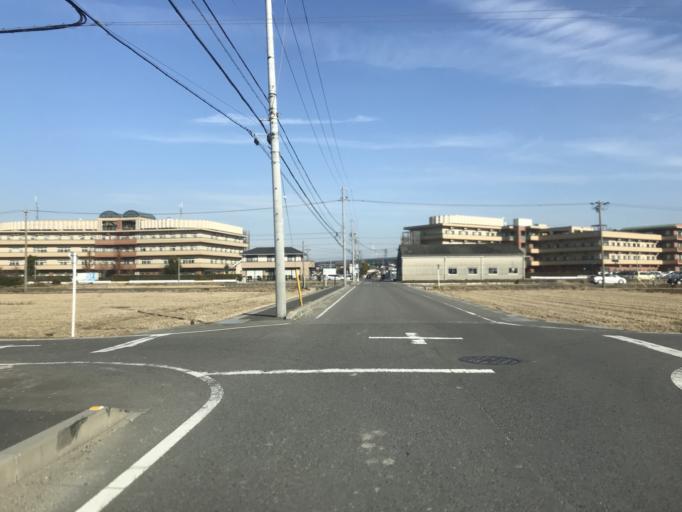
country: JP
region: Aichi
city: Iwakura
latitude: 35.2250
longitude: 136.8508
